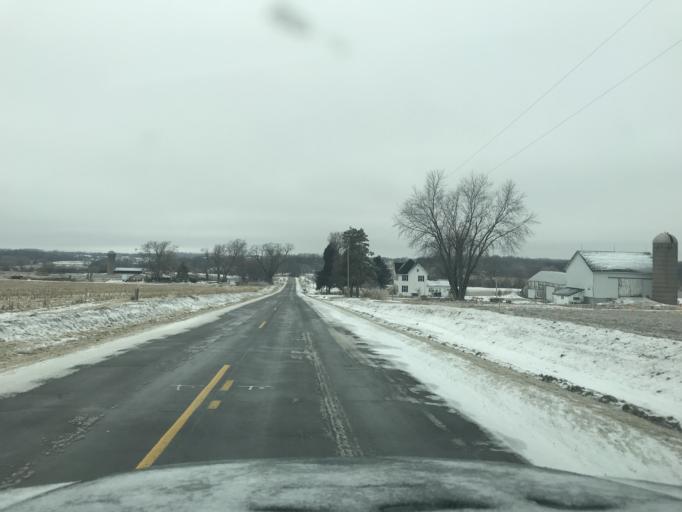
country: US
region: Wisconsin
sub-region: Dane County
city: Cottage Grove
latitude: 43.1040
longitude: -89.2351
